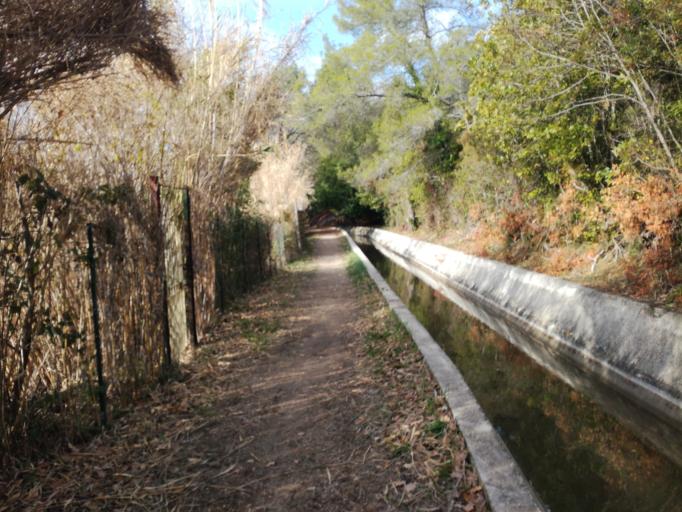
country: FR
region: Provence-Alpes-Cote d'Azur
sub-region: Departement des Alpes-Maritimes
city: Mouans-Sartoux
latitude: 43.6135
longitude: 6.9879
